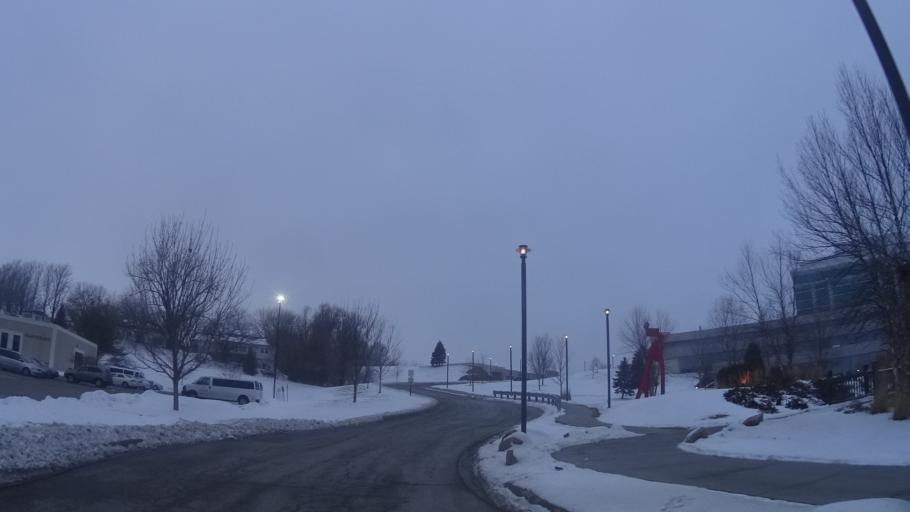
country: US
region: Nebraska
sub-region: Sarpy County
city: Offutt Air Force Base
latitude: 41.1505
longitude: -95.9199
